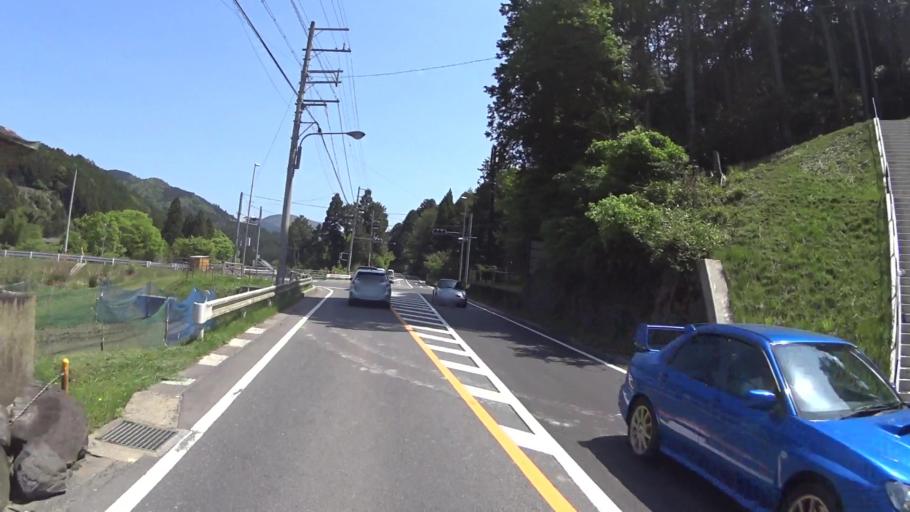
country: JP
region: Shiga Prefecture
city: Kitahama
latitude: 35.1451
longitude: 135.8408
